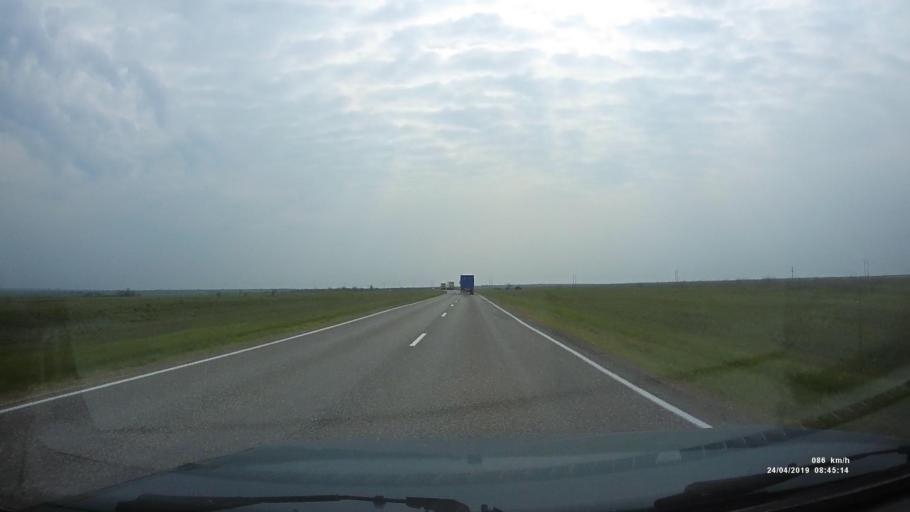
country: RU
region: Kalmykiya
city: Arshan'
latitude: 46.2366
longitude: 44.0573
